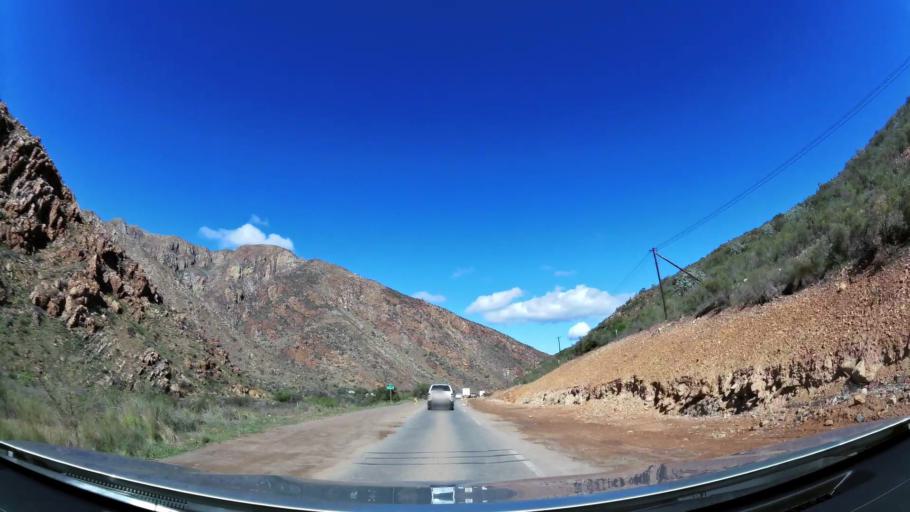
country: ZA
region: Western Cape
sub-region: Cape Winelands District Municipality
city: Ashton
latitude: -33.8073
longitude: 20.0941
